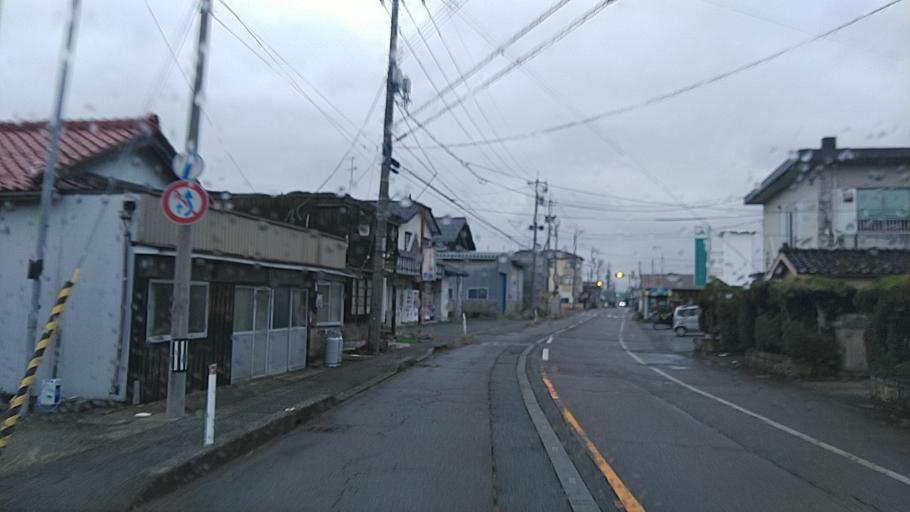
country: JP
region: Ishikawa
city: Komatsu
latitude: 36.3268
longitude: 136.3808
